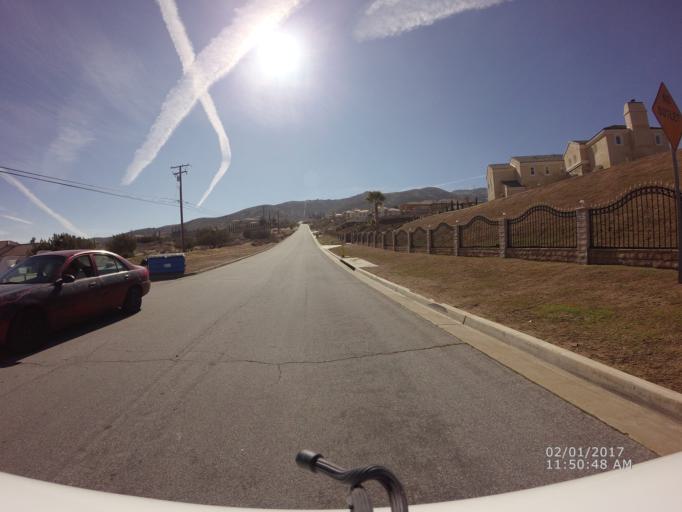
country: US
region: California
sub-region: Los Angeles County
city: Palmdale
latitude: 34.5456
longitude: -118.1327
